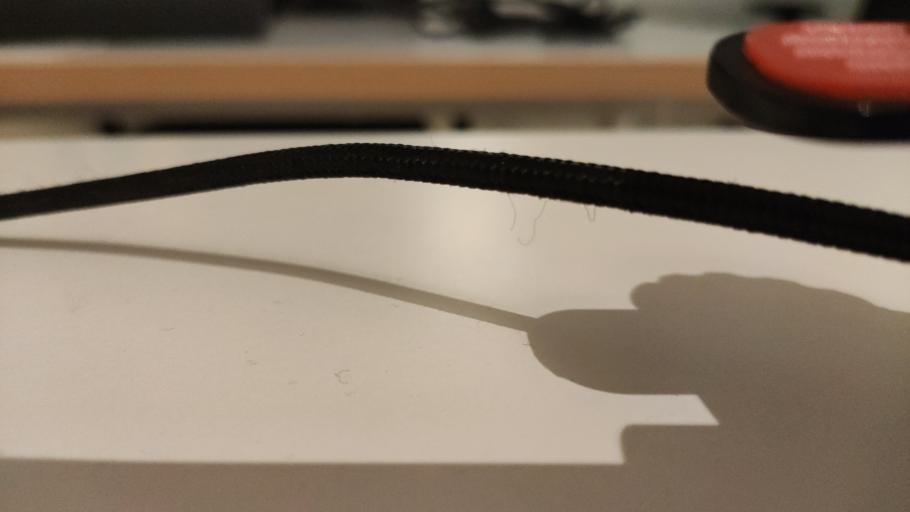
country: RU
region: Moskovskaya
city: Il'inskiy Pogost
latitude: 55.5236
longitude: 38.8720
